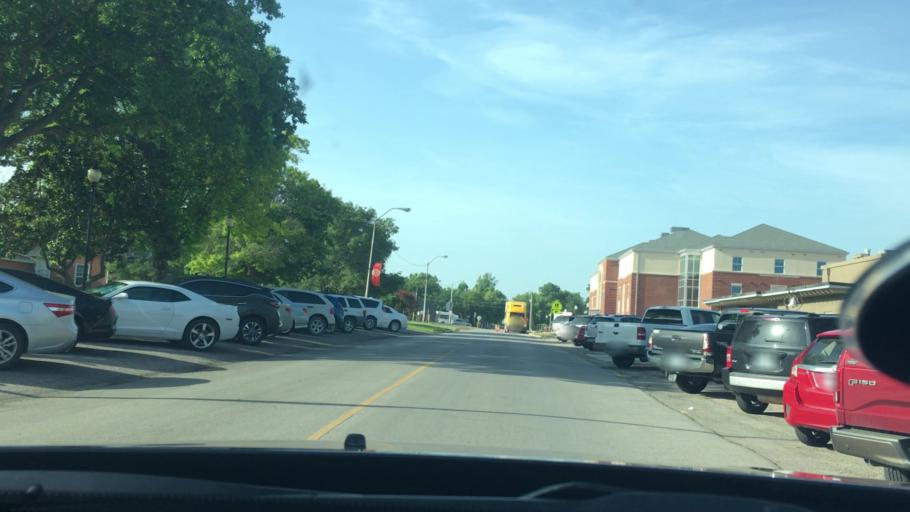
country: US
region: Oklahoma
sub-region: Pontotoc County
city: Ada
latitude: 34.7731
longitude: -96.6655
